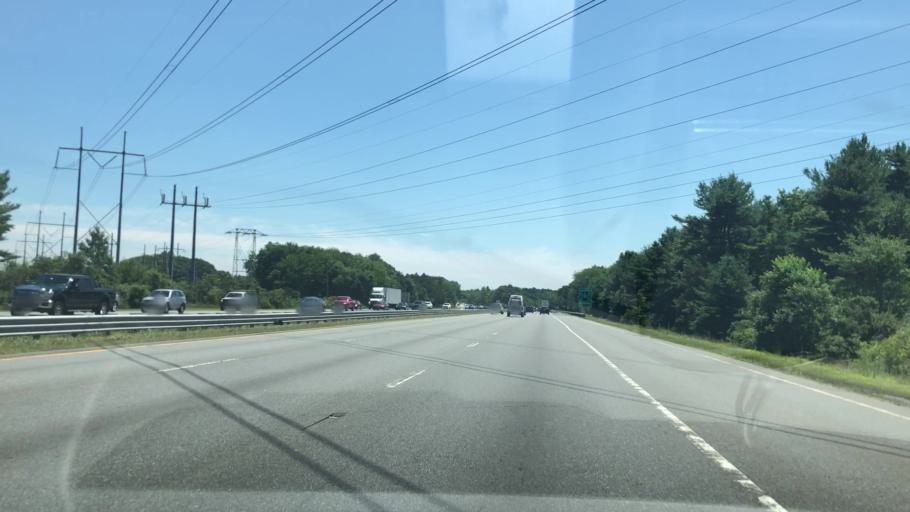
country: US
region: Massachusetts
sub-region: Middlesex County
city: Wilmington
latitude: 42.6042
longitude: -71.1719
